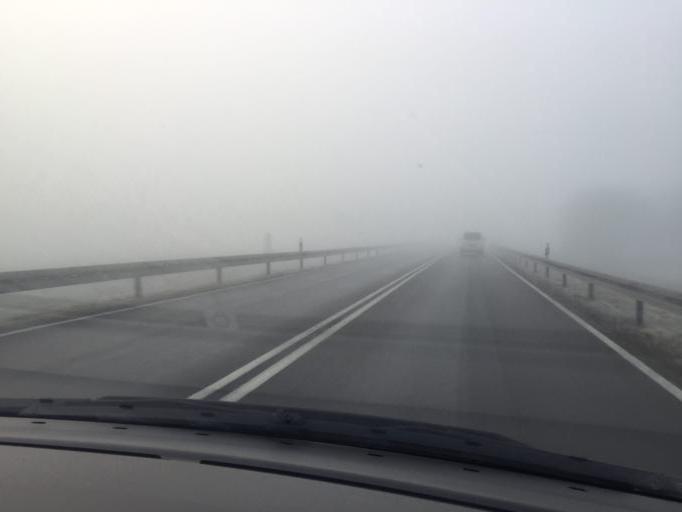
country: DE
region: Baden-Wuerttemberg
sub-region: Freiburg Region
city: Donaueschingen
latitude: 47.9392
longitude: 8.5171
